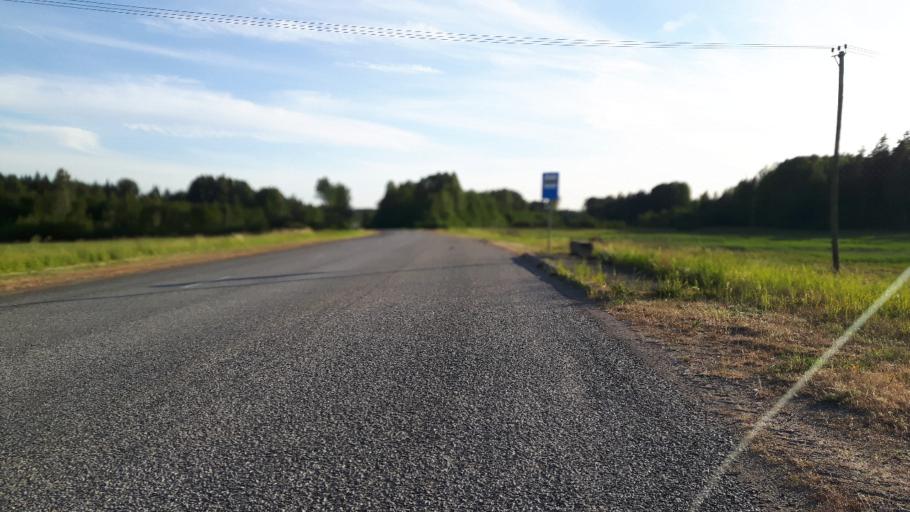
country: LV
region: Kuldigas Rajons
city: Kuldiga
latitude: 56.9925
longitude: 22.0877
